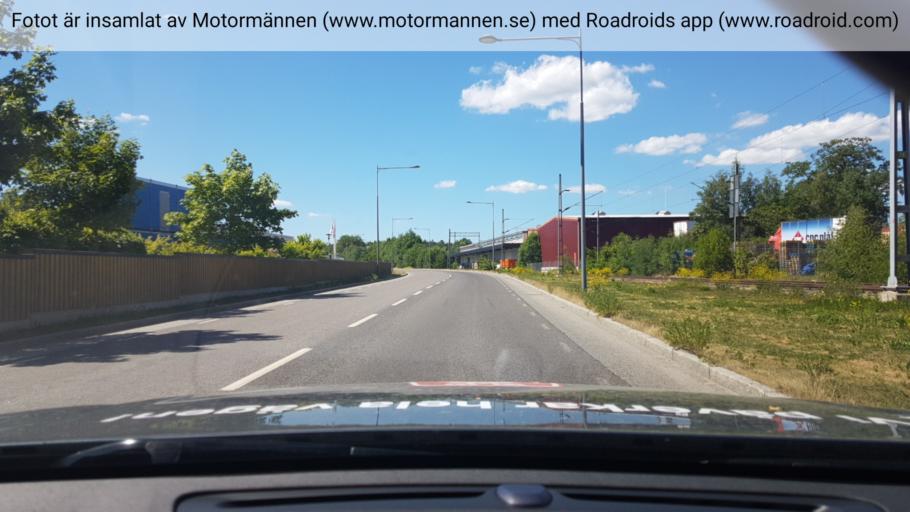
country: SE
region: Stockholm
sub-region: Jarfalla Kommun
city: Jakobsberg
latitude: 59.3873
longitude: 17.8851
